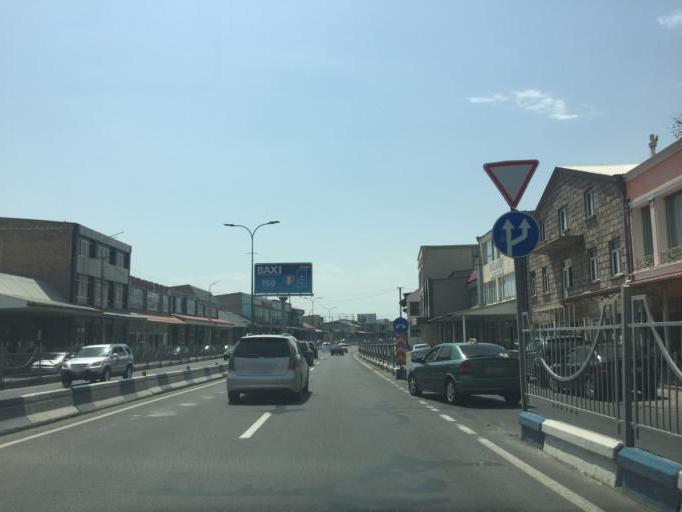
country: AM
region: Ararat
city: Argavand
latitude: 40.1589
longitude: 44.4373
